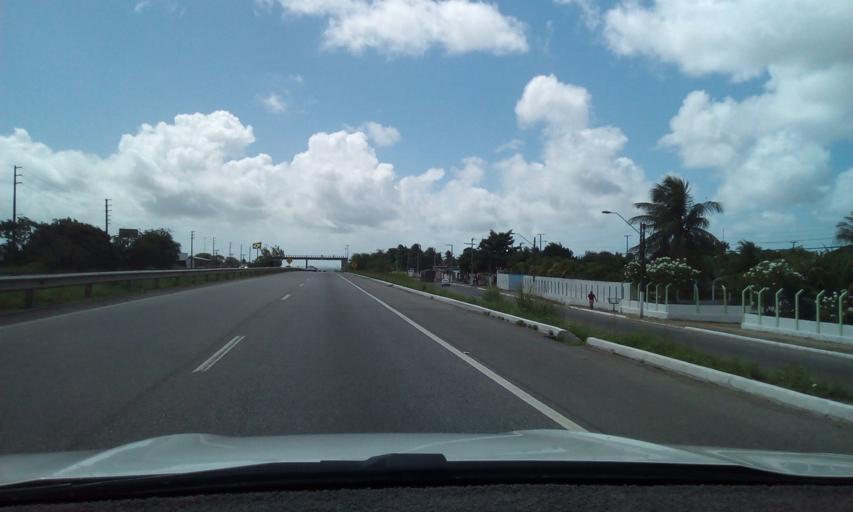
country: BR
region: Paraiba
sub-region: Bayeux
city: Bayeux
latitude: -7.1298
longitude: -34.9540
